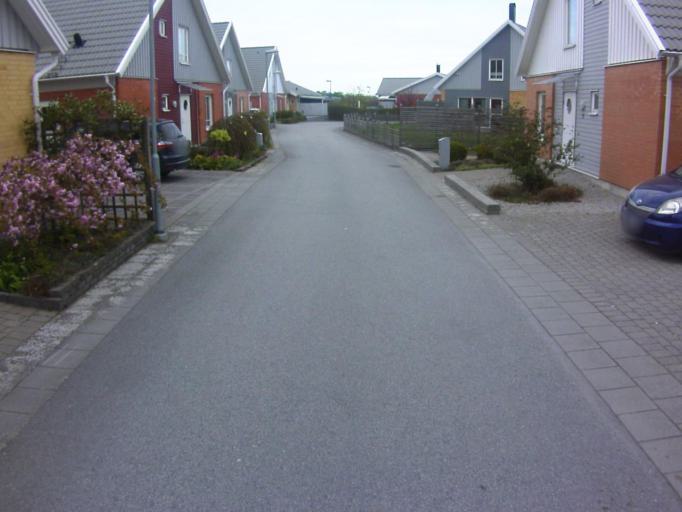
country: SE
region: Skane
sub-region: Kavlinge Kommun
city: Loddekopinge
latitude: 55.7640
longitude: 13.0223
